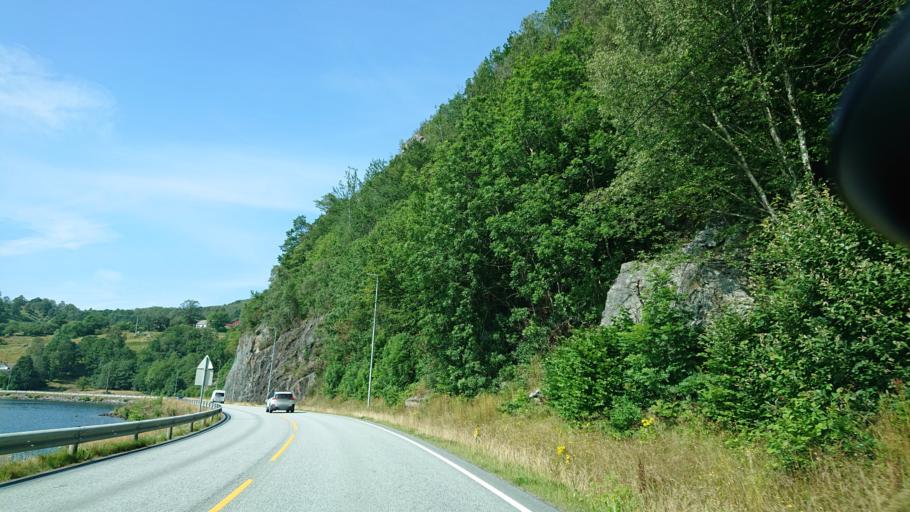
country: NO
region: Rogaland
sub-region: Strand
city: Tau
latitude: 59.0678
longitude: 5.9609
